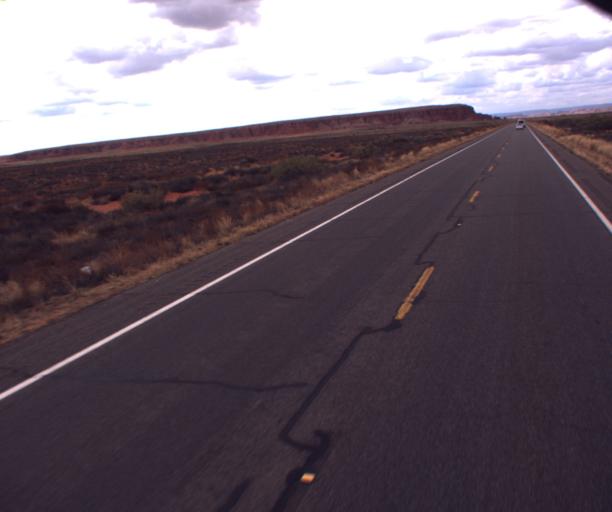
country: US
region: Arizona
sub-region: Navajo County
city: Kayenta
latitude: 36.7823
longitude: -109.9824
